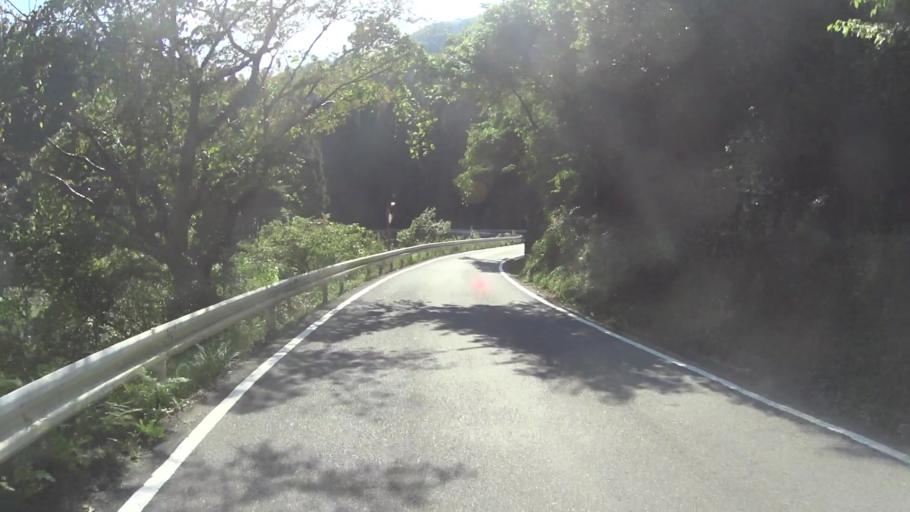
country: JP
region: Kyoto
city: Kameoka
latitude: 34.9852
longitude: 135.5750
